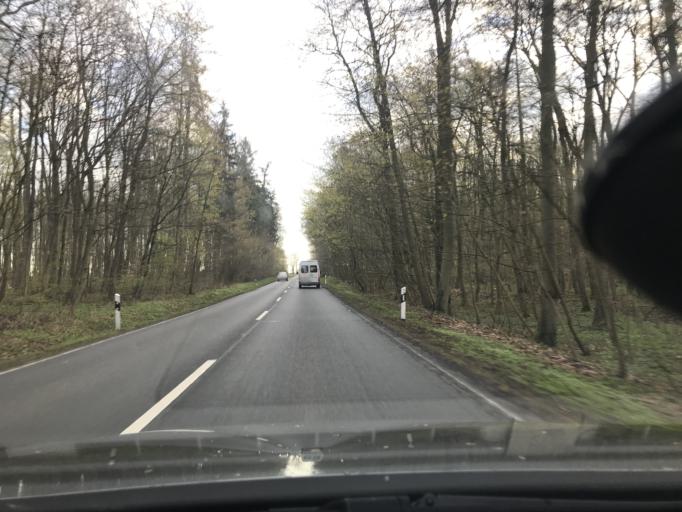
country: DE
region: Thuringia
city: Menteroda
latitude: 51.3002
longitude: 10.5560
